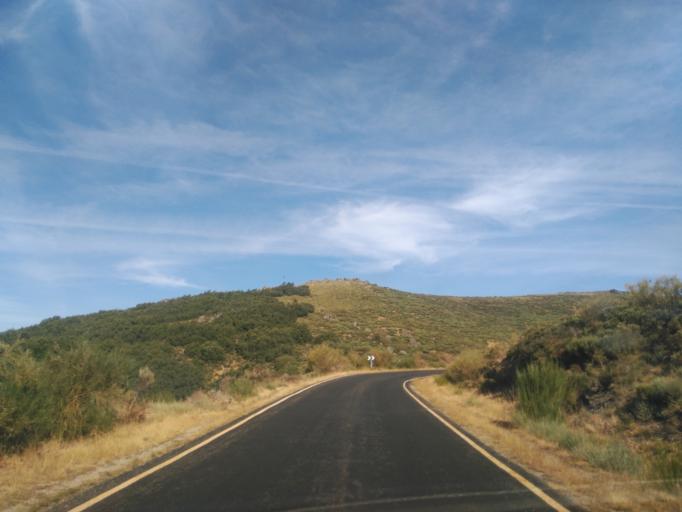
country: ES
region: Castille and Leon
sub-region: Provincia de Zamora
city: Cobreros
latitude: 42.1467
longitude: -6.7304
